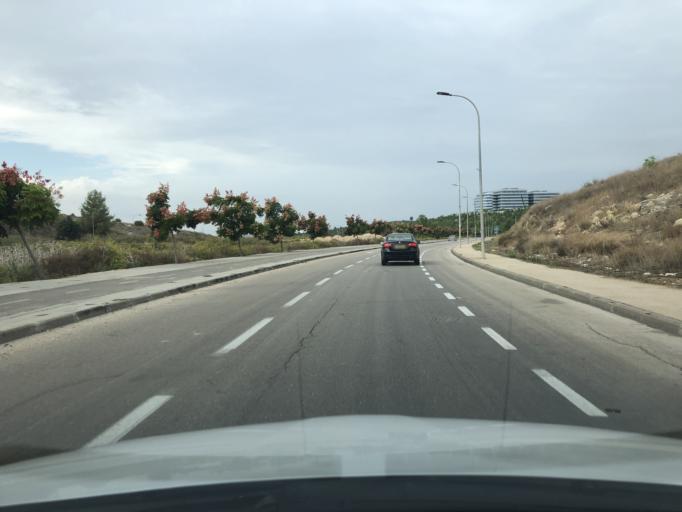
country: PS
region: West Bank
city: Al Midyah
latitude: 31.9190
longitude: 34.9975
